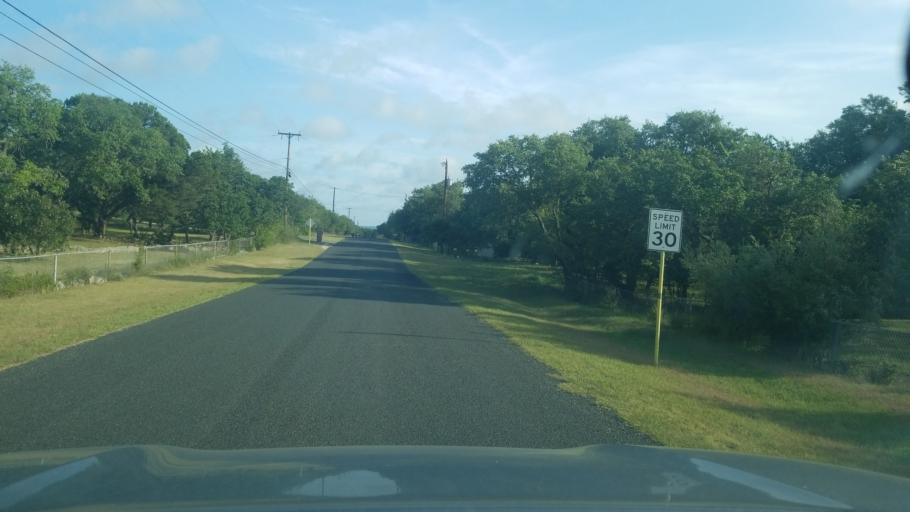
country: US
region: Texas
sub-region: Bexar County
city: Timberwood Park
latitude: 29.7032
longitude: -98.5168
